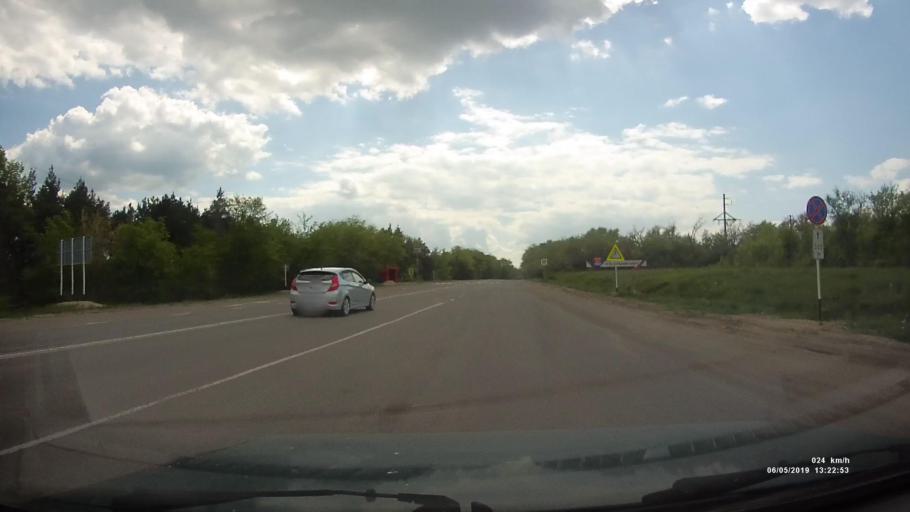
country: RU
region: Rostov
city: Ust'-Donetskiy
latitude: 47.6939
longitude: 40.9232
